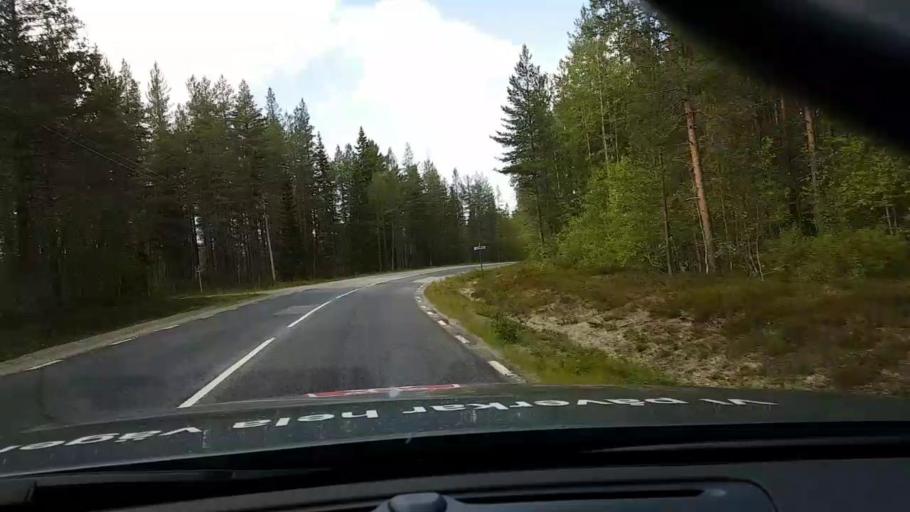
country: SE
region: Vaesterbotten
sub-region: Asele Kommun
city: Asele
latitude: 63.7929
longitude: 17.5784
